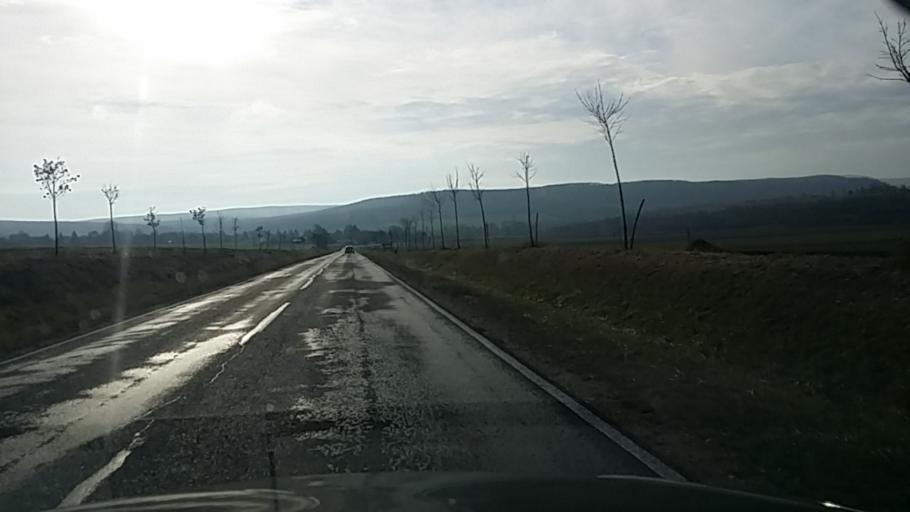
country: HU
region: Veszprem
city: Urkut
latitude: 46.9748
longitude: 17.6270
